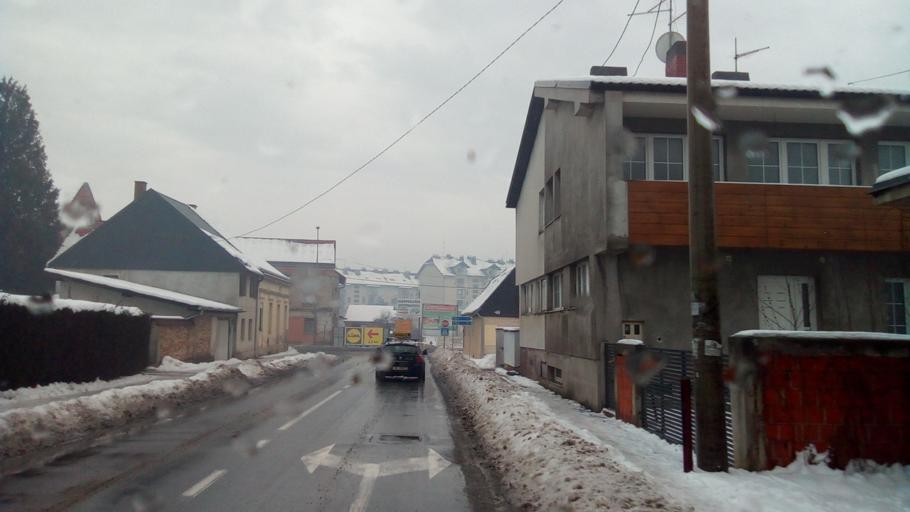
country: HR
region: Sisacko-Moslavacka
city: Petrinja
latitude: 45.4405
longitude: 16.2682
